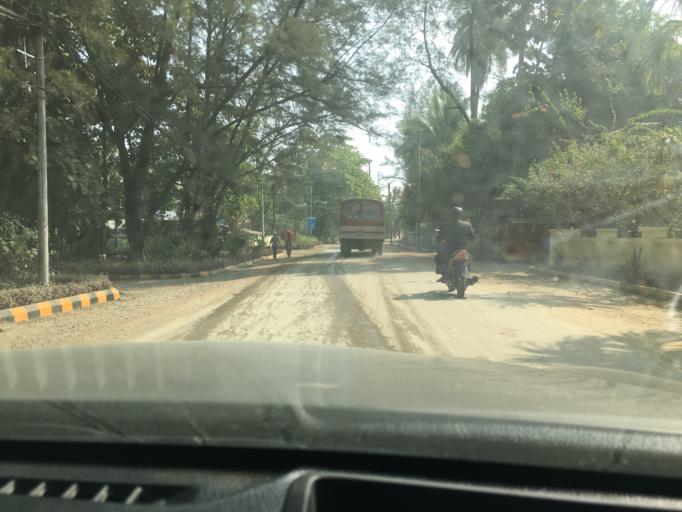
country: MM
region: Bago
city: Pyay
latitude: 18.4706
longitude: 94.3650
